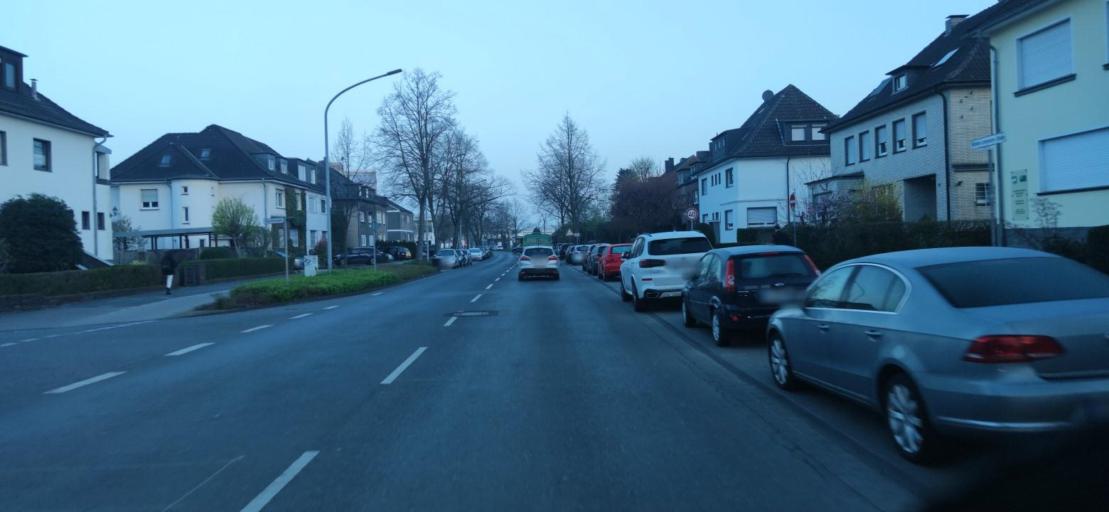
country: DE
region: North Rhine-Westphalia
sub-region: Regierungsbezirk Dusseldorf
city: Dinslaken
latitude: 51.5670
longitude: 6.7355
